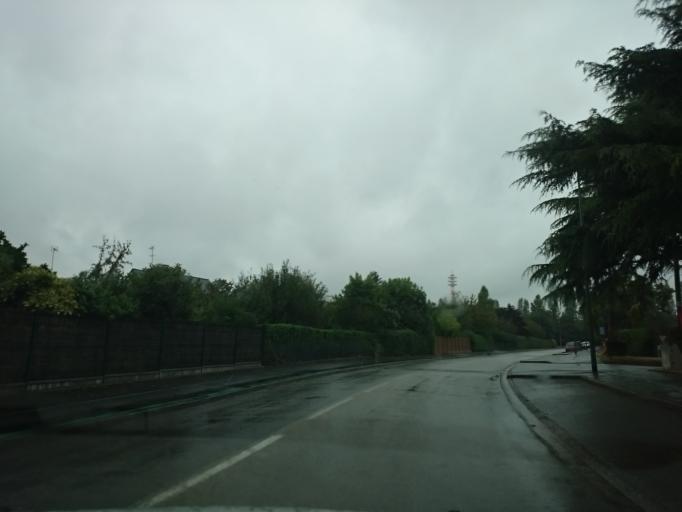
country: FR
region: Brittany
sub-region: Departement d'Ille-et-Vilaine
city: Cesson-Sevigne
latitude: 48.1156
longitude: -1.6235
